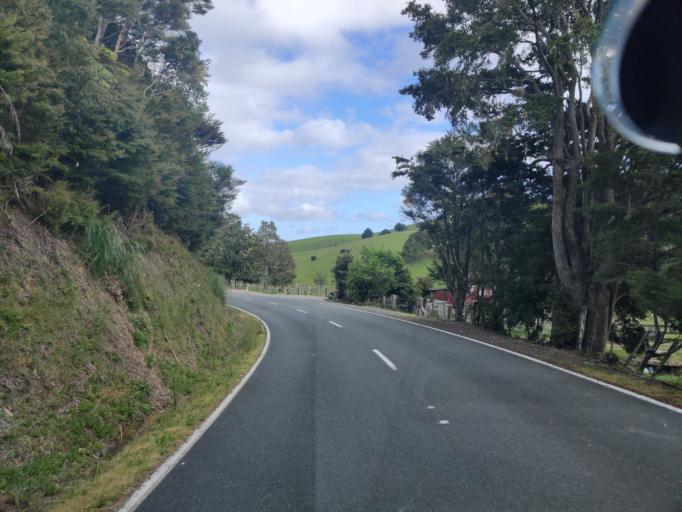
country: NZ
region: Northland
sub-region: Whangarei
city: Ngunguru
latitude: -35.5777
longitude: 174.4043
